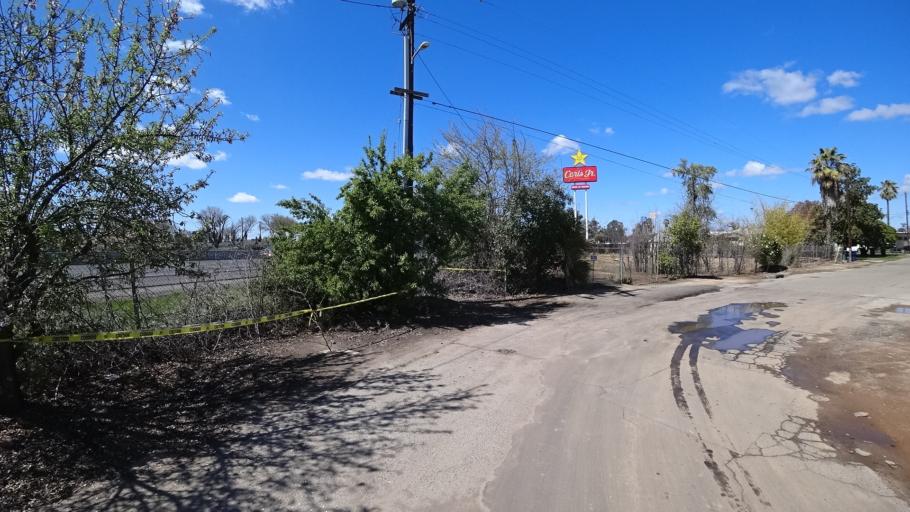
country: US
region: California
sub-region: Fresno County
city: West Park
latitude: 36.8064
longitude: -119.8837
